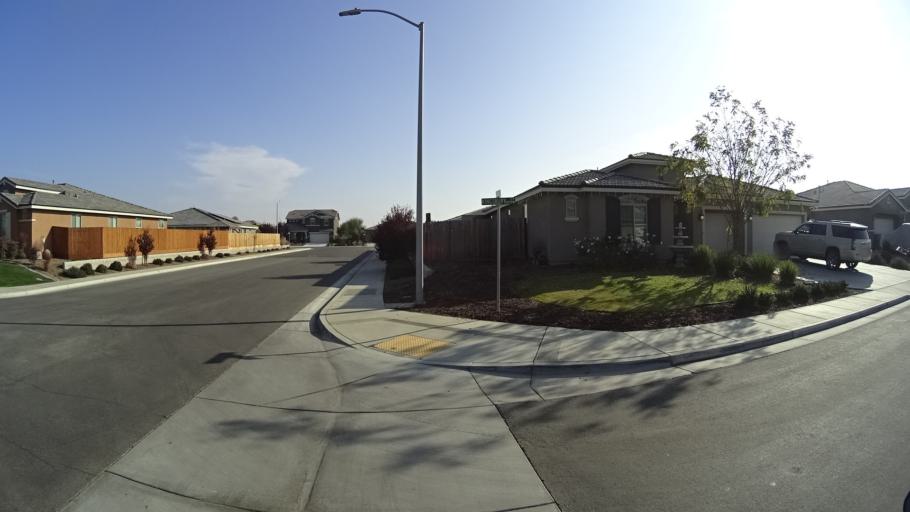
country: US
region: California
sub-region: Kern County
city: Rosedale
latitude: 35.3520
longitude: -119.1711
